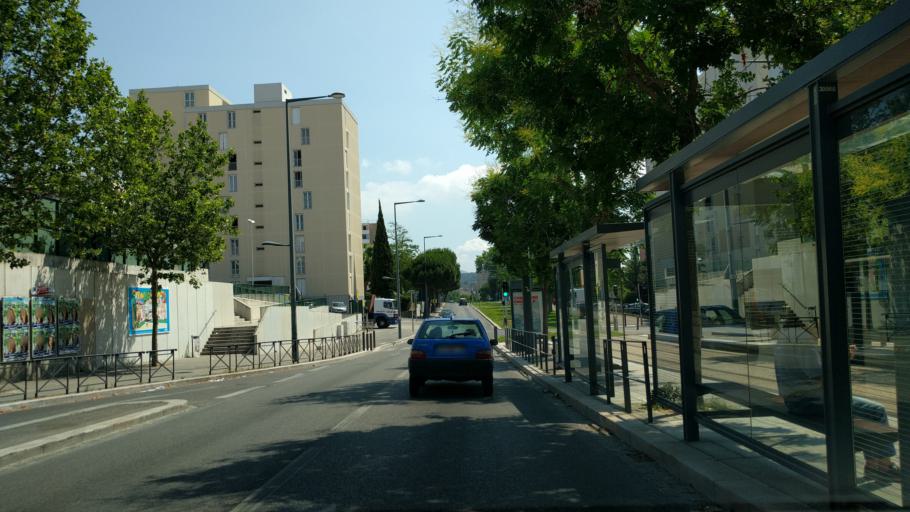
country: FR
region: Provence-Alpes-Cote d'Azur
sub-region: Departement des Bouches-du-Rhone
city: Marseille 11
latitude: 43.2927
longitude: 5.4367
